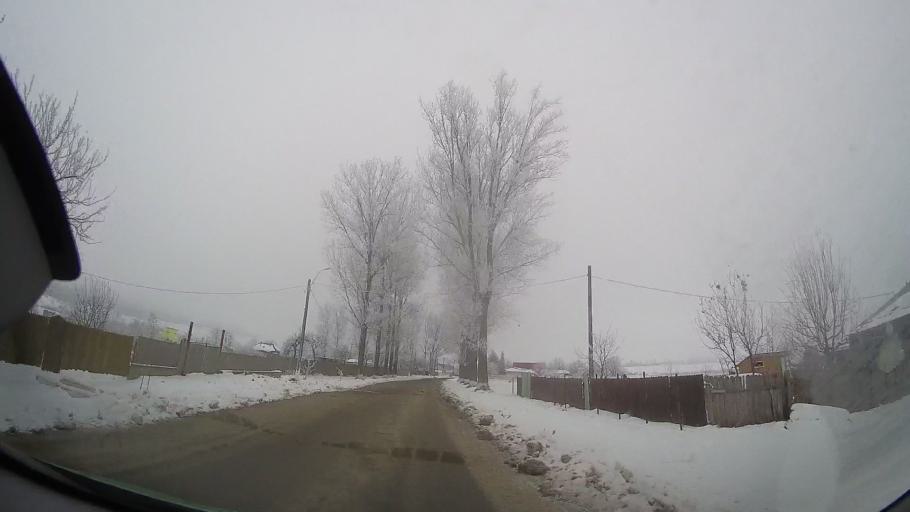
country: RO
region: Iasi
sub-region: Comuna Tansa
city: Tansa
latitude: 46.9139
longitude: 27.2100
